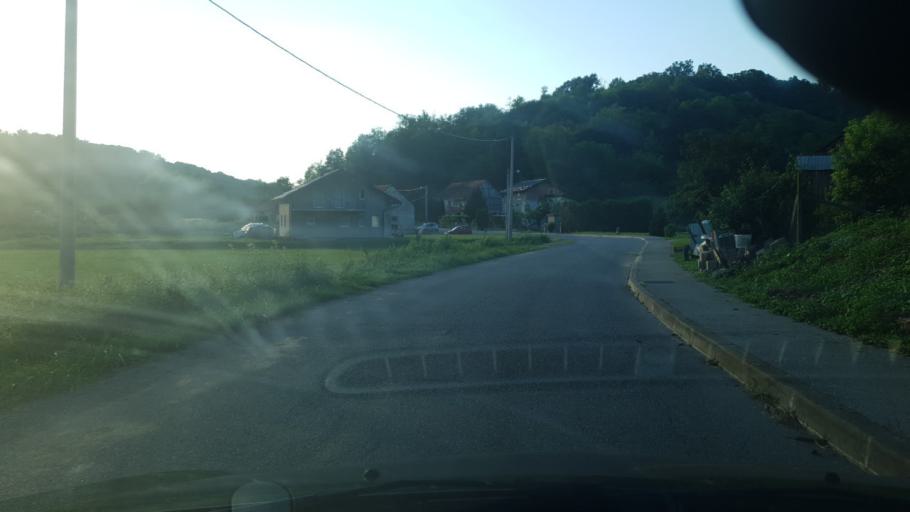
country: HR
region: Krapinsko-Zagorska
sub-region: Grad Krapina
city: Krapina
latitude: 46.1301
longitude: 15.8631
